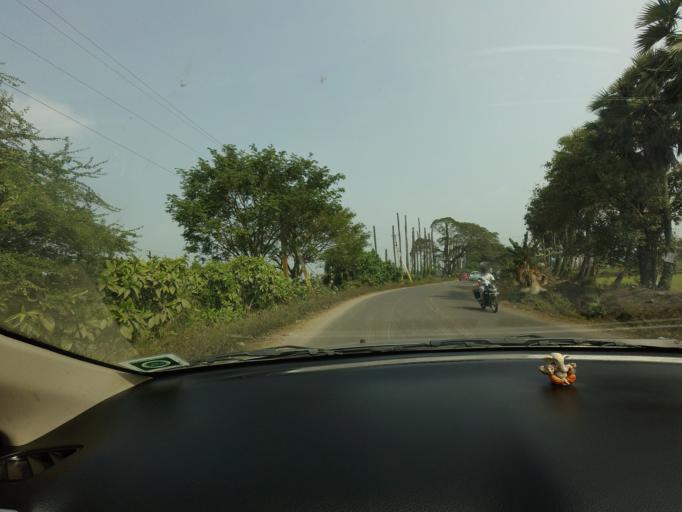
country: IN
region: Andhra Pradesh
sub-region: Krishna
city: Kankipadu
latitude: 16.4547
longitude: 80.7788
